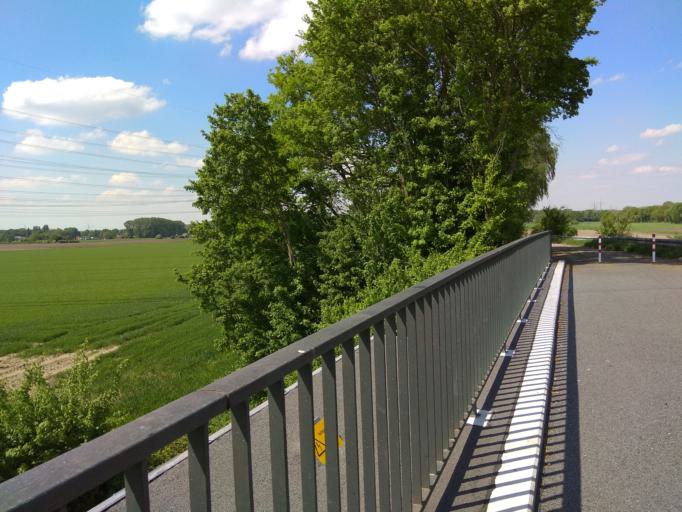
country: DE
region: North Rhine-Westphalia
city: Marl
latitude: 51.6297
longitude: 7.0754
